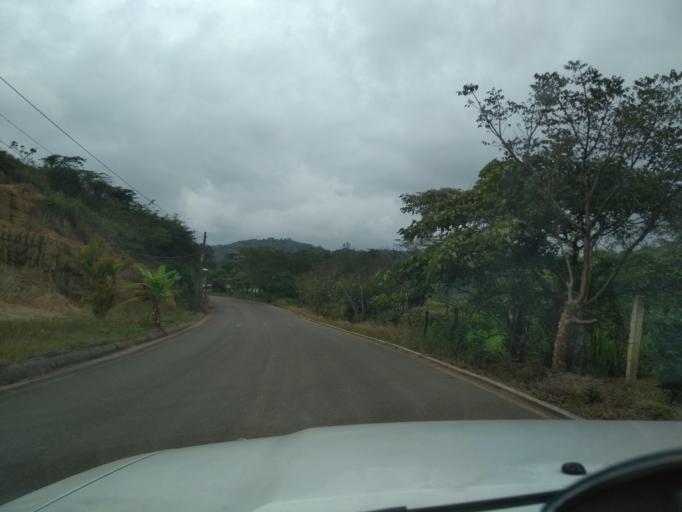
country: MX
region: Veracruz
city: El Castillo
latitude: 19.5481
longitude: -96.8470
